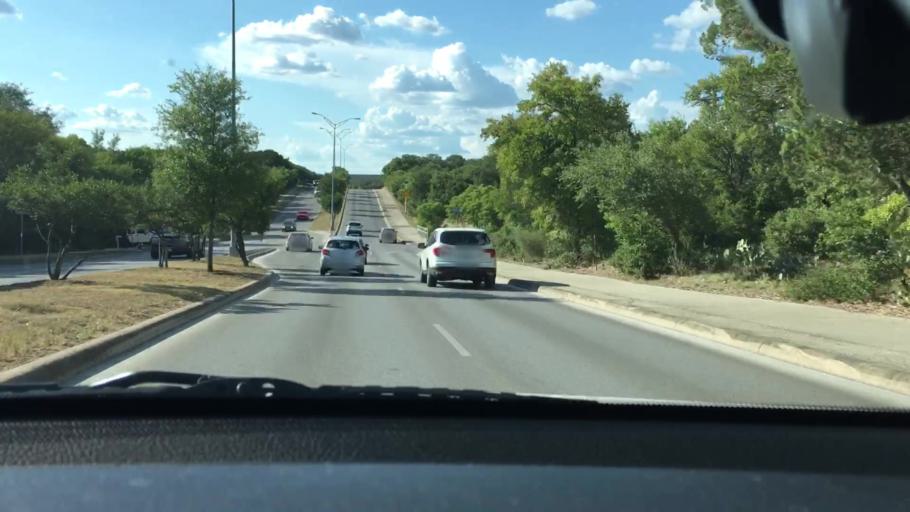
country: US
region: Texas
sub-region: Bexar County
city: Selma
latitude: 29.5862
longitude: -98.2874
